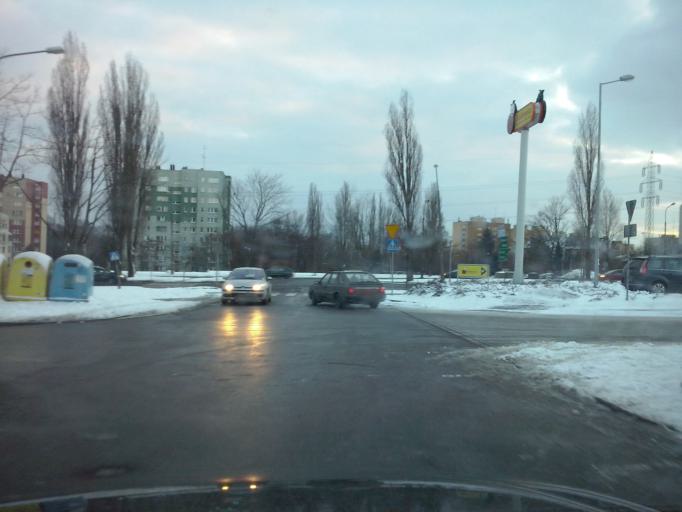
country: PL
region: Lesser Poland Voivodeship
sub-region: Krakow
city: Krakow
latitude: 50.0876
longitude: 20.0074
